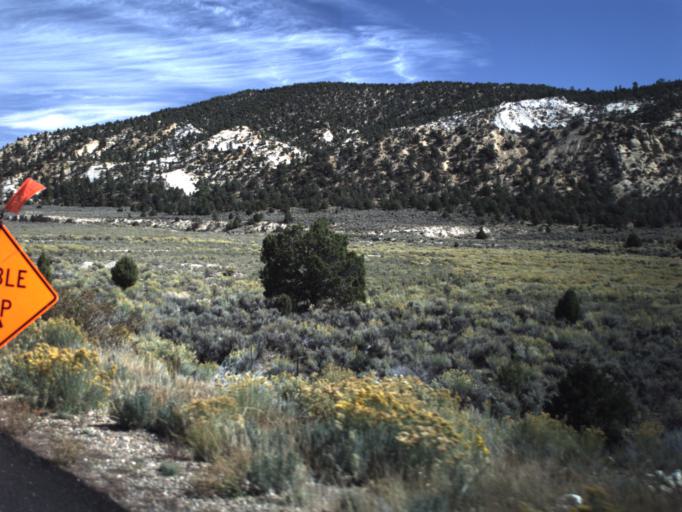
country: US
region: Utah
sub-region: Garfield County
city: Panguitch
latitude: 37.7023
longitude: -111.7906
